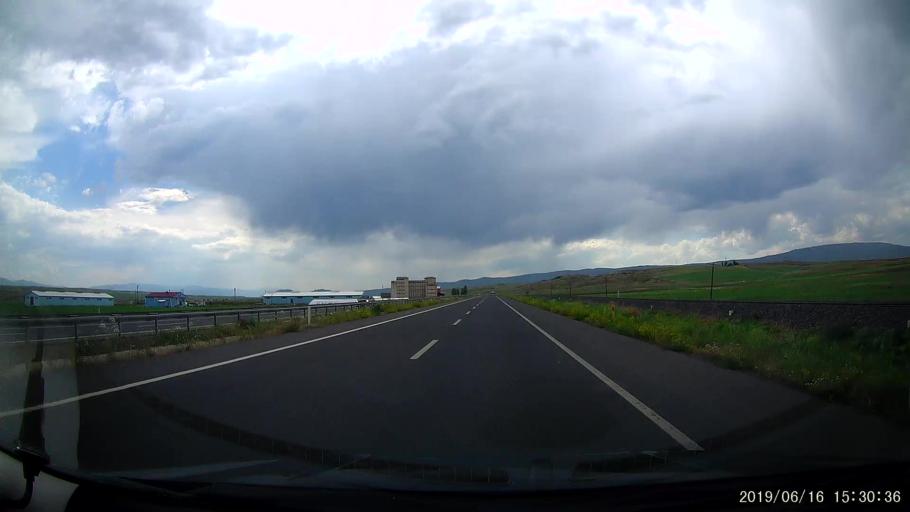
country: TR
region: Erzurum
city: Horasan
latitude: 40.0340
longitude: 42.1009
